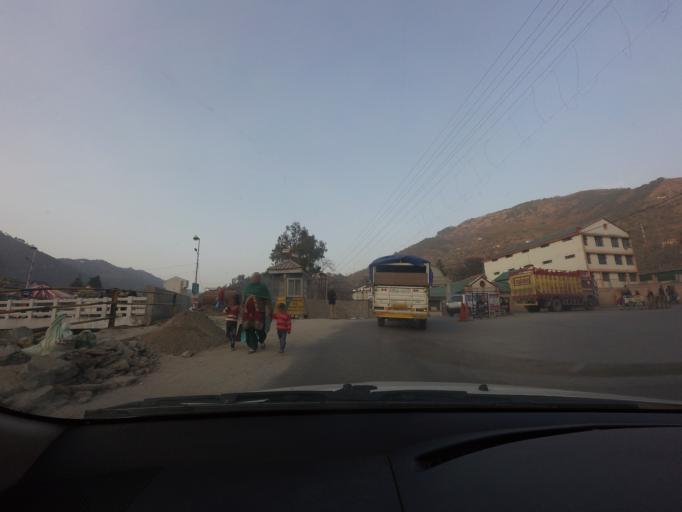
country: IN
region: Himachal Pradesh
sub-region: Mandi
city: Mandi
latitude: 31.7063
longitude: 76.9350
